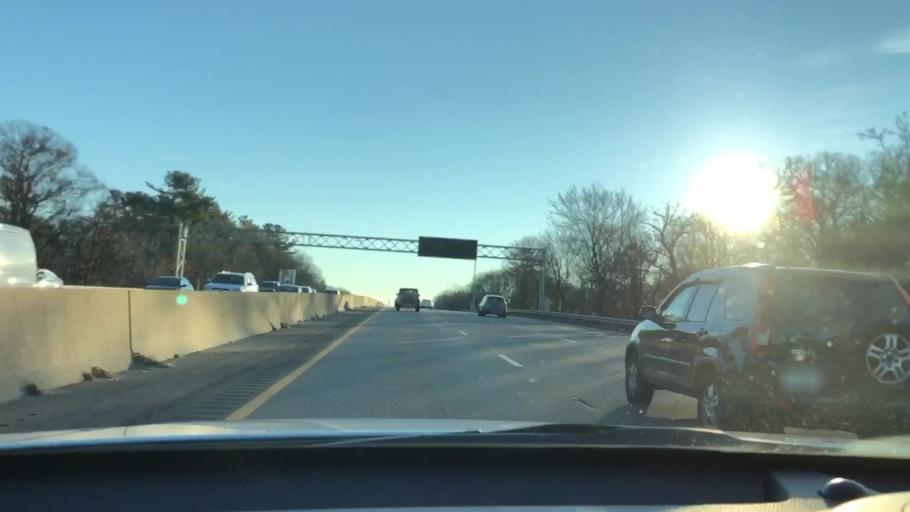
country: US
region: Massachusetts
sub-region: Norfolk County
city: Braintree
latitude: 42.2036
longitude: -70.9864
